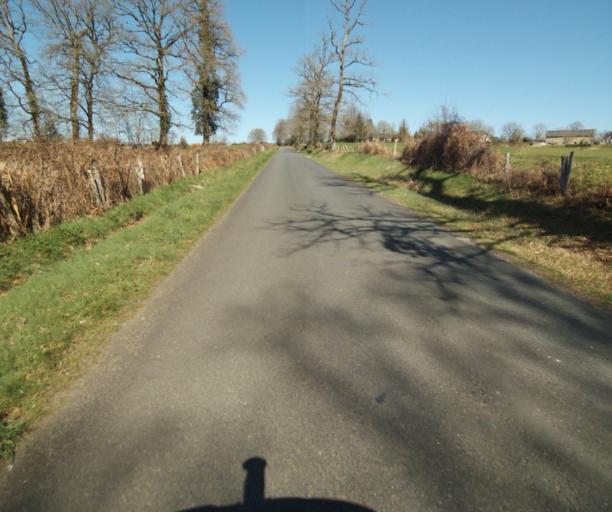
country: FR
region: Limousin
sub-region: Departement de la Correze
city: Saint-Clement
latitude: 45.3330
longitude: 1.6560
